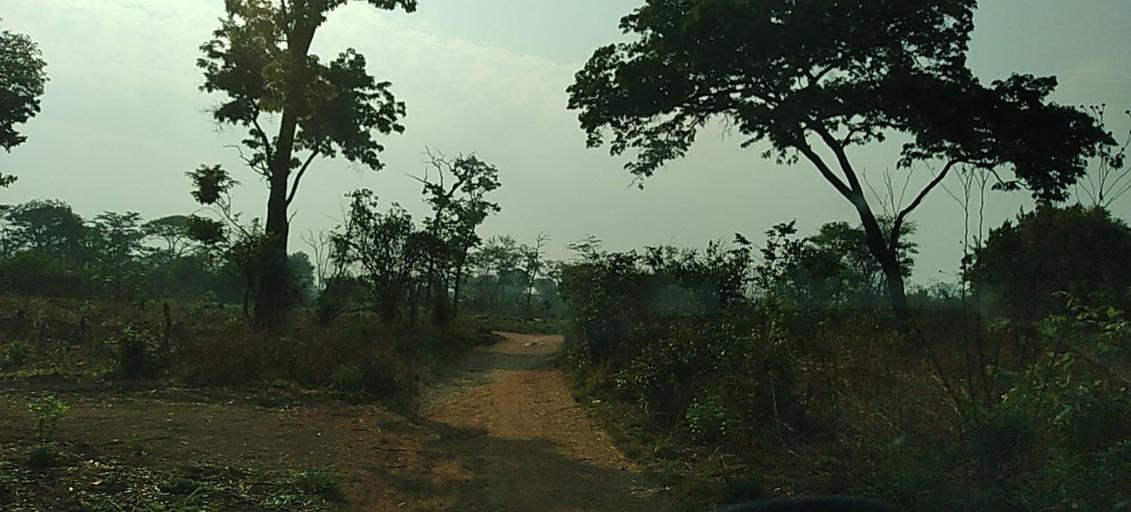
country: ZM
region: North-Western
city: Solwezi
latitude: -12.3563
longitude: 26.5471
